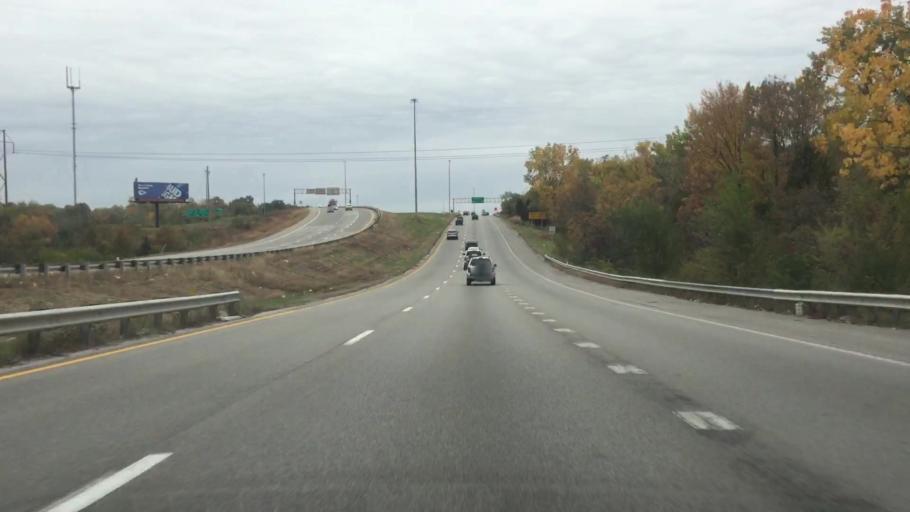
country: US
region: Missouri
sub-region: Jackson County
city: Raytown
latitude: 39.0136
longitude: -94.4931
